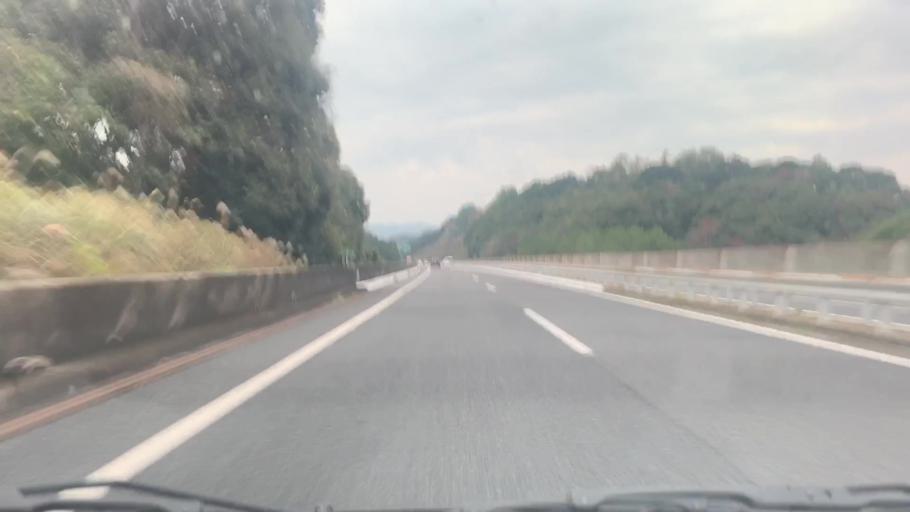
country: JP
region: Nagasaki
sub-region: Isahaya-shi
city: Isahaya
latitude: 32.8198
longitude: 129.9816
